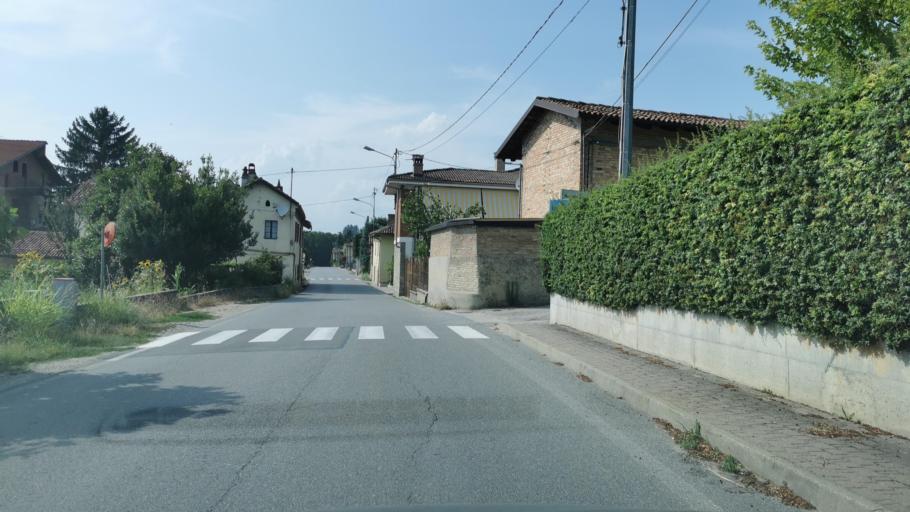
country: IT
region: Piedmont
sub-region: Provincia di Cuneo
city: Grinzane Cavour
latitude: 44.6448
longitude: 7.9986
